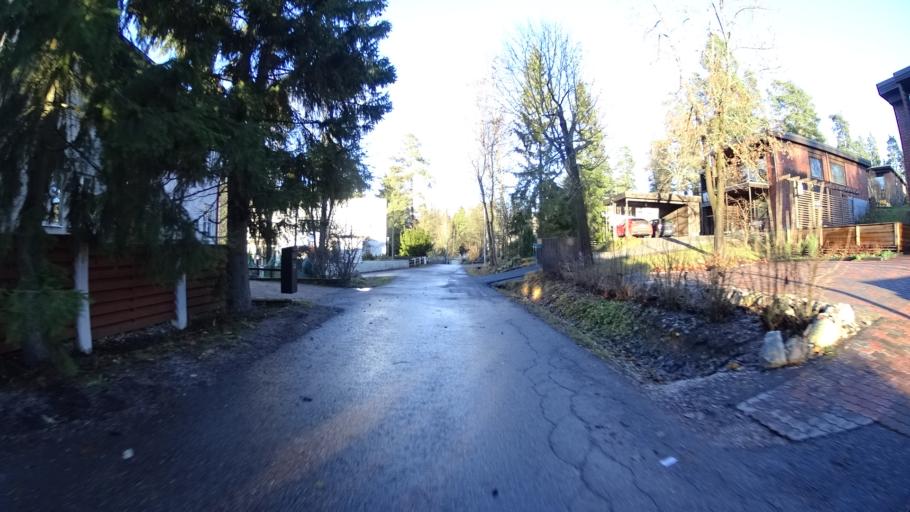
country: FI
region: Uusimaa
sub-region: Helsinki
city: Kauniainen
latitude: 60.2115
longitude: 24.7385
